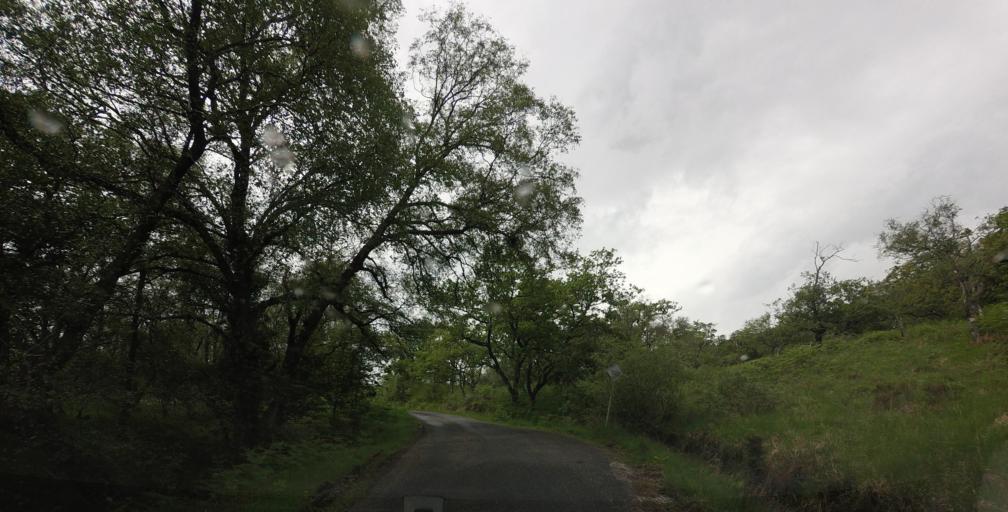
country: GB
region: Scotland
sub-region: Highland
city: Fort William
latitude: 56.7755
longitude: -5.2061
